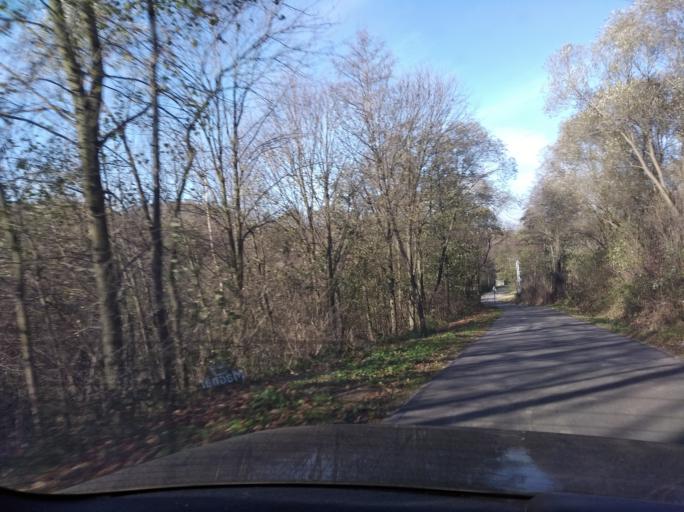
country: PL
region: Subcarpathian Voivodeship
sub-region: Powiat ropczycko-sedziszowski
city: Wielopole Skrzynskie
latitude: 49.9009
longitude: 21.5712
